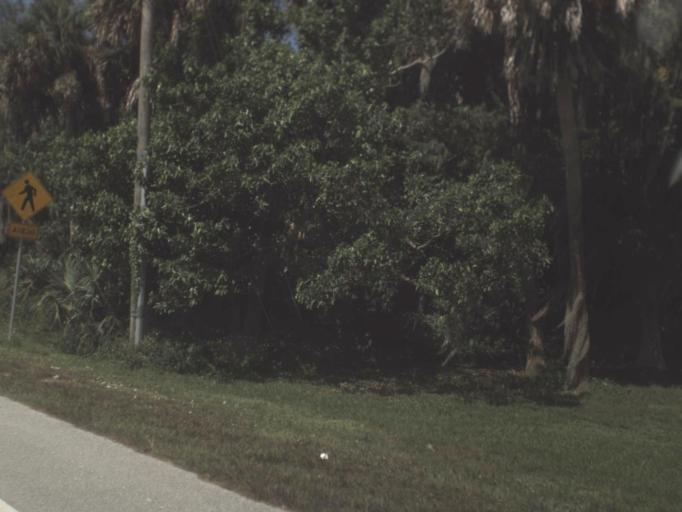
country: US
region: Florida
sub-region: Okeechobee County
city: Taylor Creek
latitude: 27.1867
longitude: -80.7427
